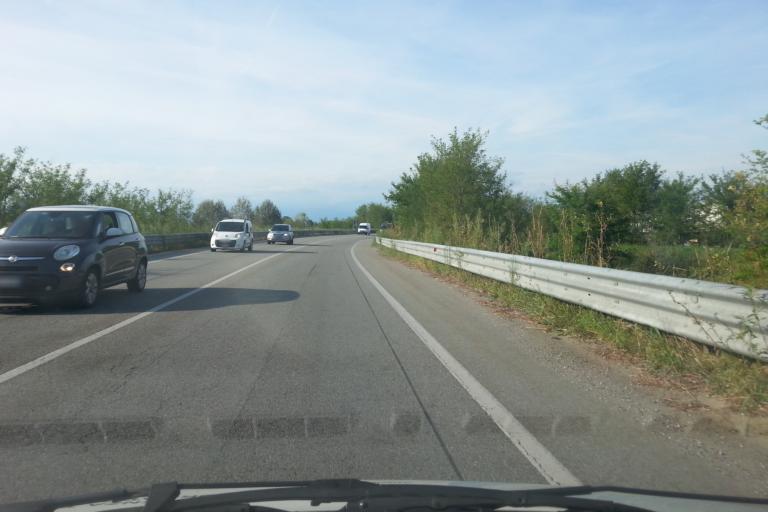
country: IT
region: Piedmont
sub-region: Provincia di Torino
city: San Raffaele Cimena
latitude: 45.1455
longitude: 7.8384
